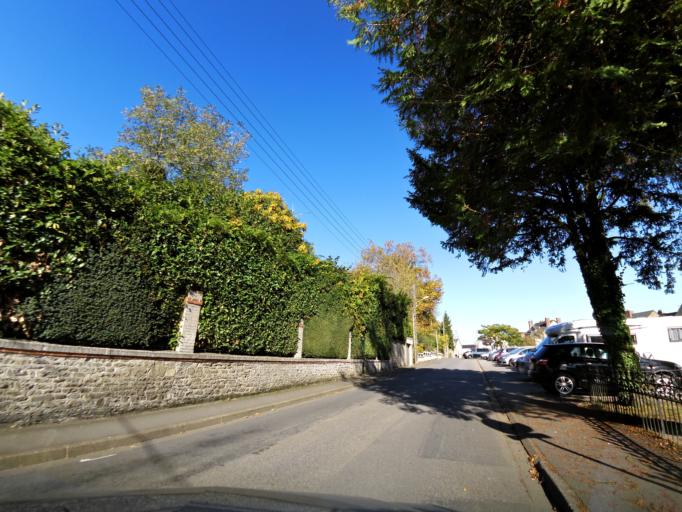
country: FR
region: Brittany
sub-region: Departement d'Ille-et-Vilaine
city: Bain-de-Bretagne
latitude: 47.8412
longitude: -1.6840
